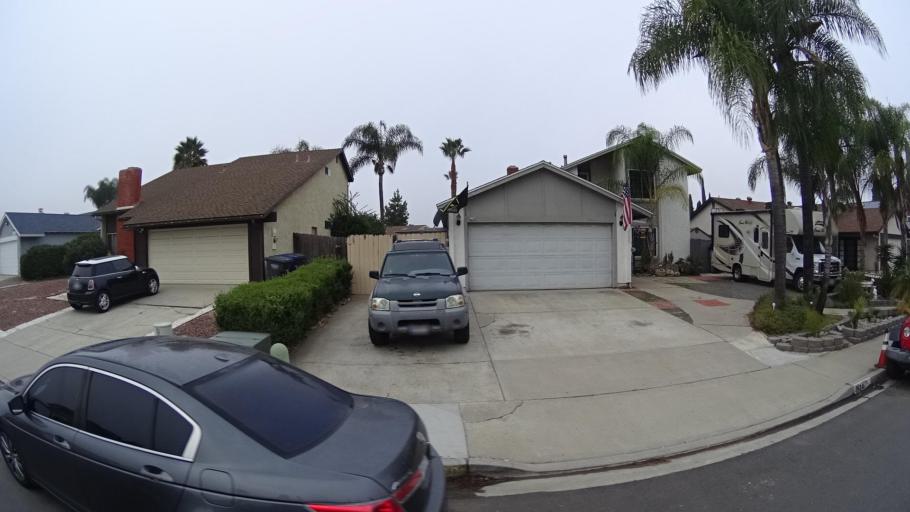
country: US
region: California
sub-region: San Diego County
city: Rancho San Diego
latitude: 32.7298
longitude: -116.9596
